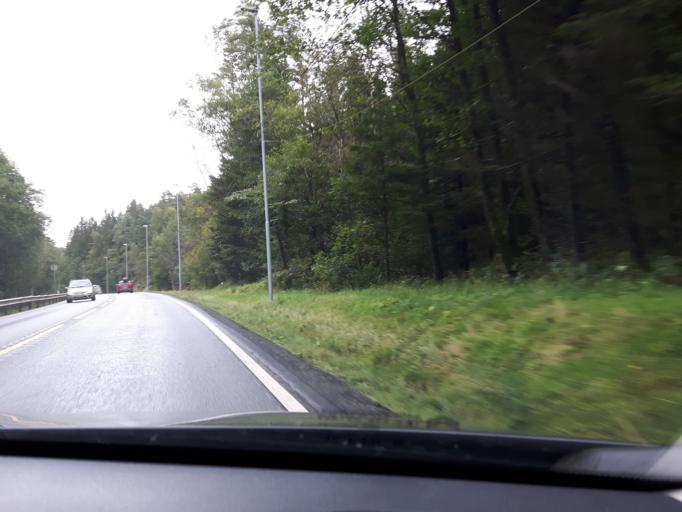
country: NO
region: Vest-Agder
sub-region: Marnardal
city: Helland
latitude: 58.0831
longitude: 7.6166
